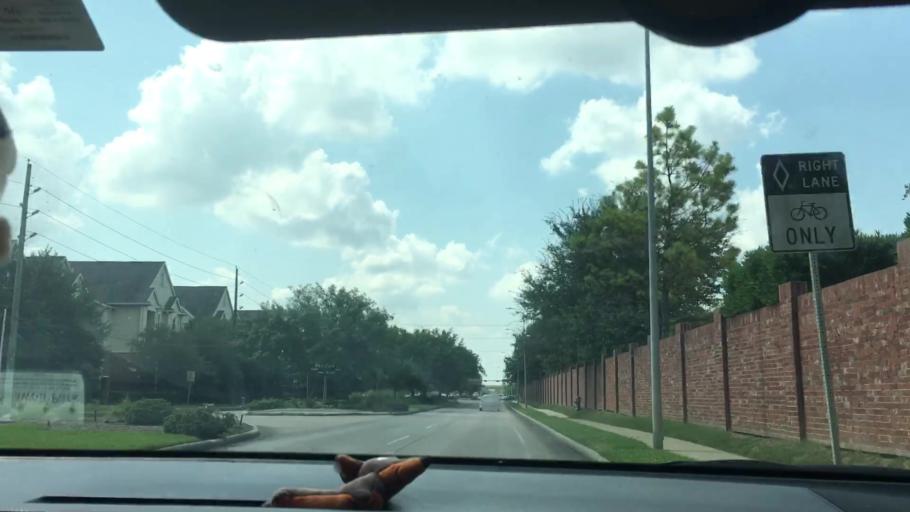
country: US
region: Texas
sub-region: Harris County
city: Bunker Hill Village
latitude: 29.7226
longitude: -95.5717
